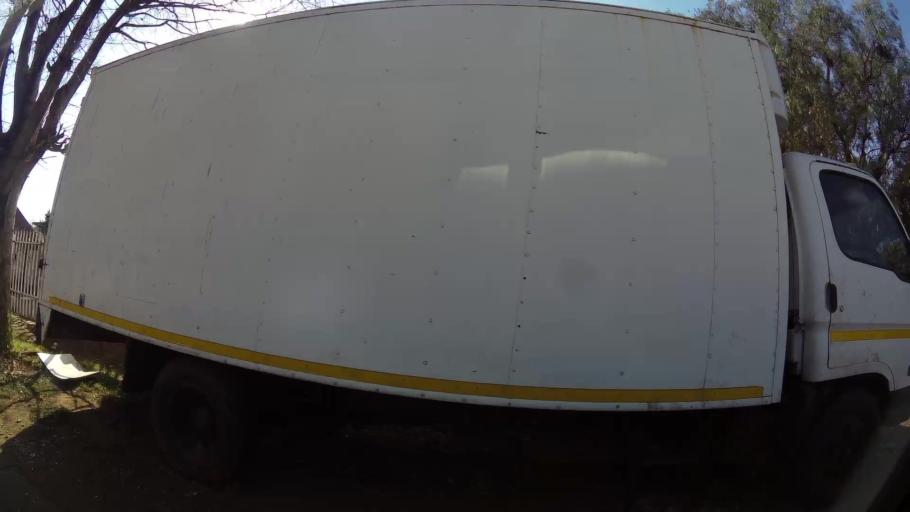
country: ZA
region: Gauteng
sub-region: Ekurhuleni Metropolitan Municipality
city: Boksburg
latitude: -26.2494
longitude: 28.3067
